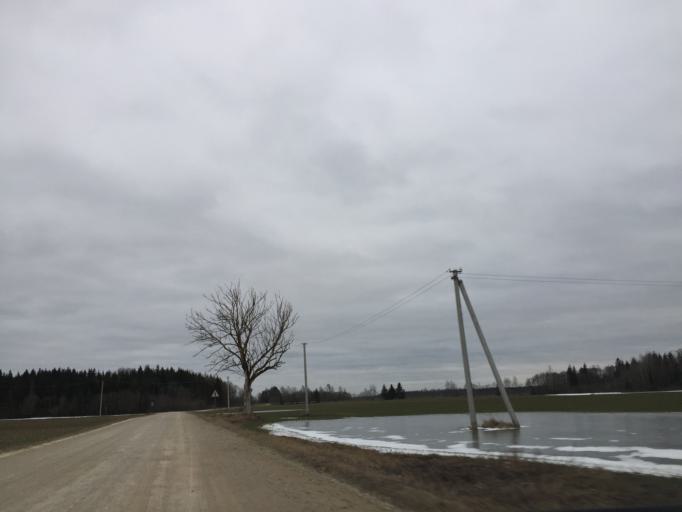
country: LT
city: Zagare
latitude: 56.2928
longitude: 23.2605
